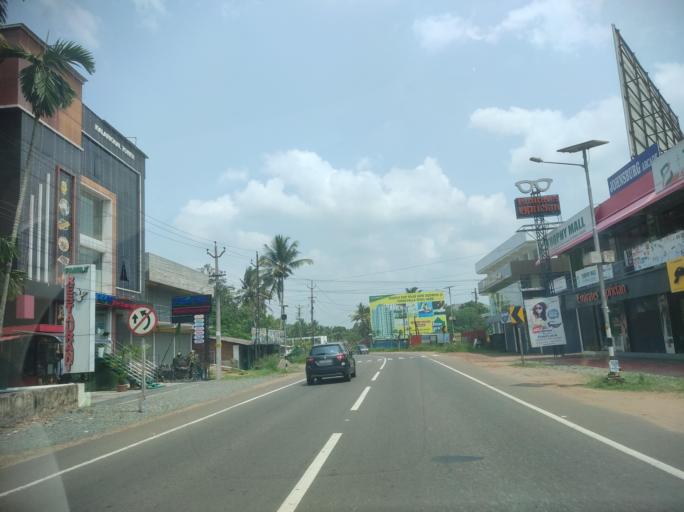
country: IN
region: Kerala
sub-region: Kottayam
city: Changanacheri
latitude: 9.4133
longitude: 76.5532
